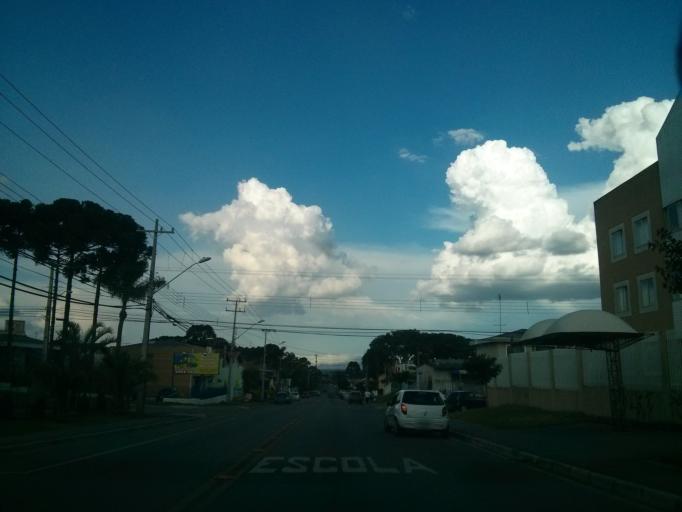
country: BR
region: Parana
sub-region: Sao Jose Dos Pinhais
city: Sao Jose dos Pinhais
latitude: -25.5134
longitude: -49.2405
